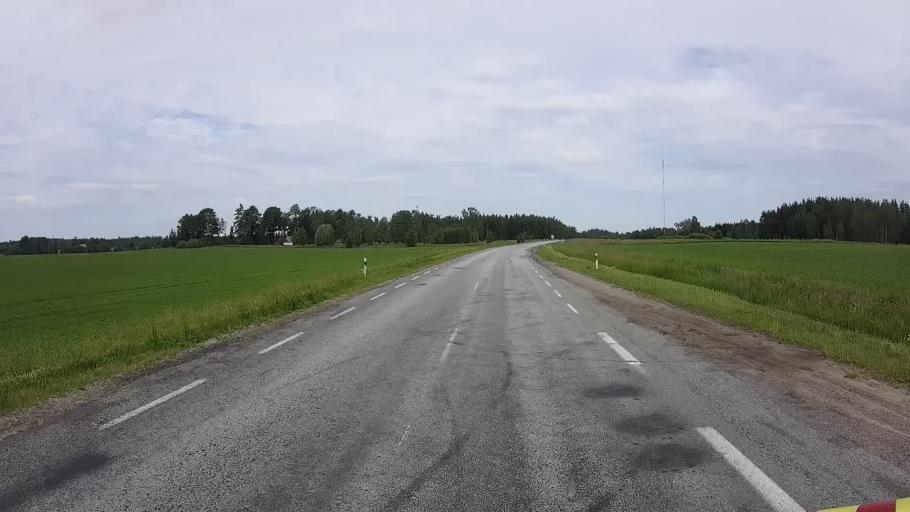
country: EE
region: Viljandimaa
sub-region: Karksi vald
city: Karksi-Nuia
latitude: 58.2302
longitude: 25.6030
